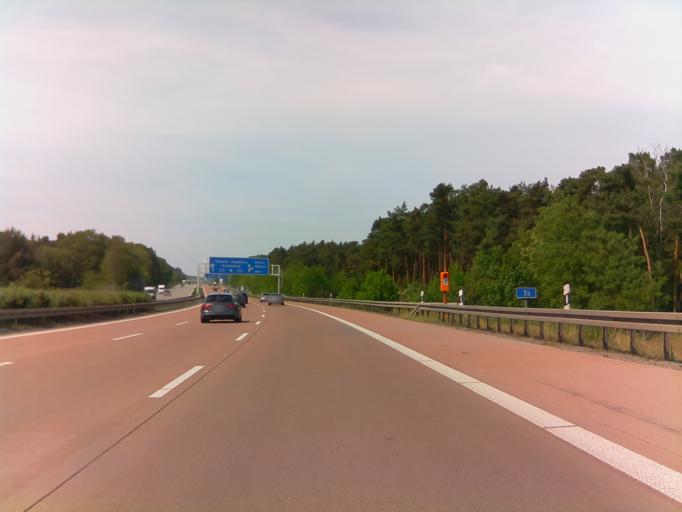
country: DE
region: Brandenburg
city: Gross Kreutz
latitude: 52.3404
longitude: 12.7147
